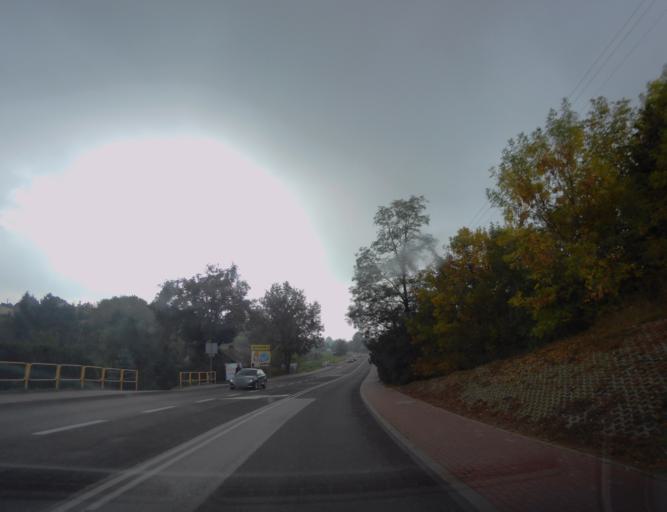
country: PL
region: Lublin Voivodeship
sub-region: Powiat krasnostawski
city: Krasnystaw
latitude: 50.9906
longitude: 23.1849
